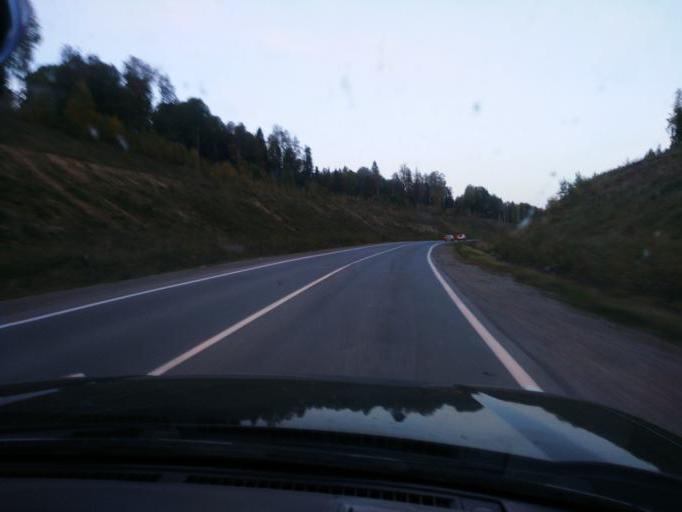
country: RU
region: Perm
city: Sylva
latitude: 58.2953
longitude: 56.8111
